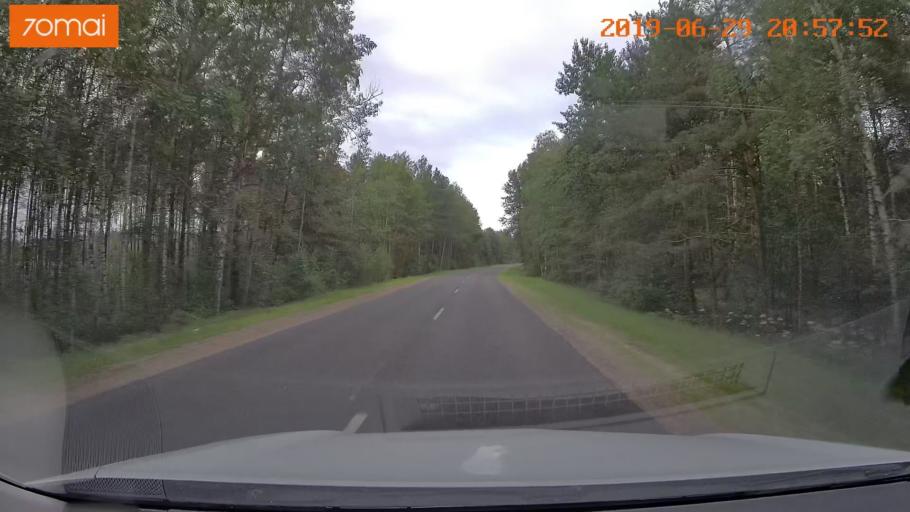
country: BY
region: Brest
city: Hantsavichy
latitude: 52.7245
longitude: 26.3759
